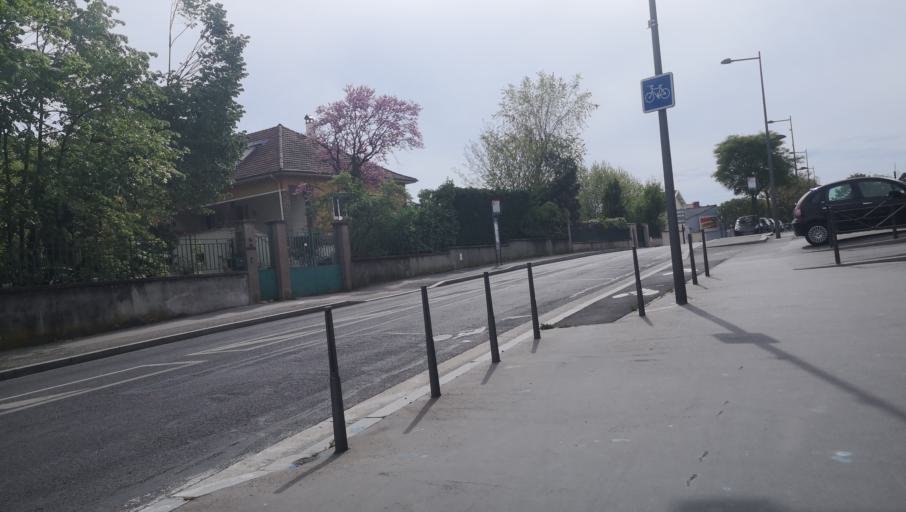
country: FR
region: Rhone-Alpes
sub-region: Departement du Rhone
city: Bron
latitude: 45.7369
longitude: 4.9166
